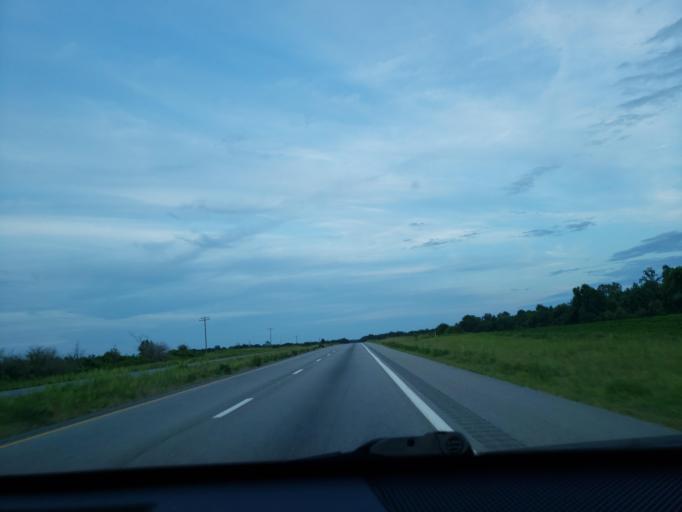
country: US
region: Virginia
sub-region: Southampton County
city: Courtland
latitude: 36.7031
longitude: -77.2658
